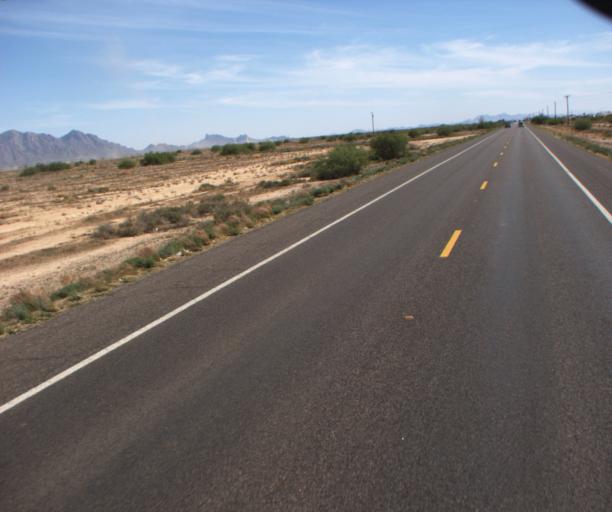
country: US
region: Arizona
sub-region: Pinal County
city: Eloy
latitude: 32.8165
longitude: -111.5154
